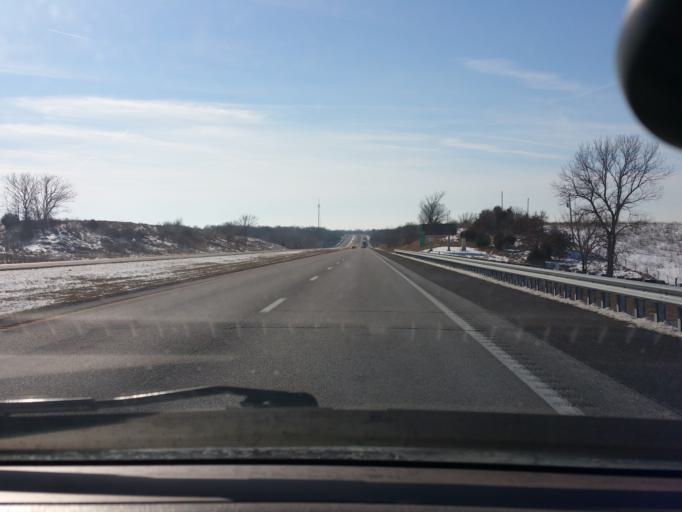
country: US
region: Missouri
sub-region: Clinton County
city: Cameron
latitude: 39.8852
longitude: -94.1600
